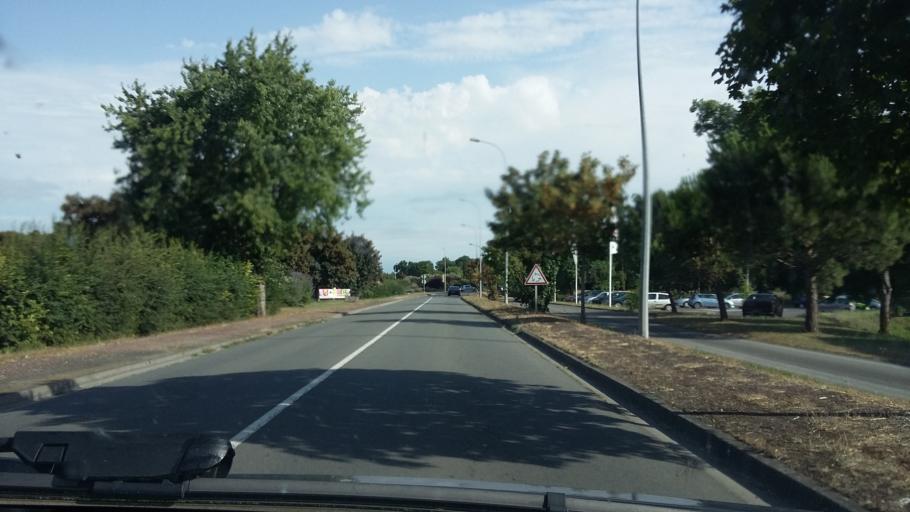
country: FR
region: Poitou-Charentes
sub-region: Departement de la Charente
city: Rouillac
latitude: 45.7782
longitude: -0.0605
